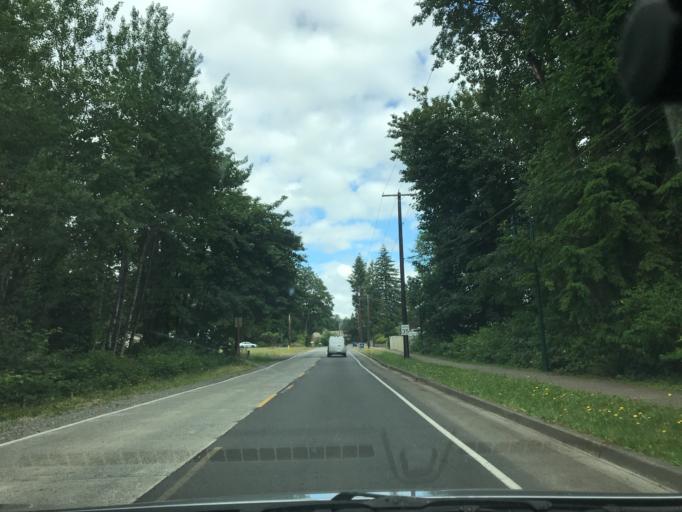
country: US
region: Washington
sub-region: King County
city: Black Diamond
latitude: 47.3121
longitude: -122.0172
